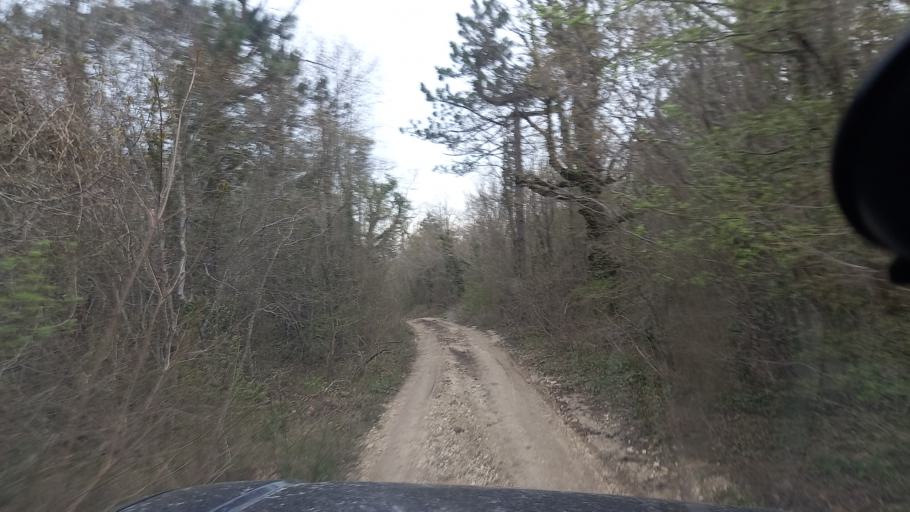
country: RU
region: Krasnodarskiy
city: Dzhubga
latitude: 44.3155
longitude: 38.6791
